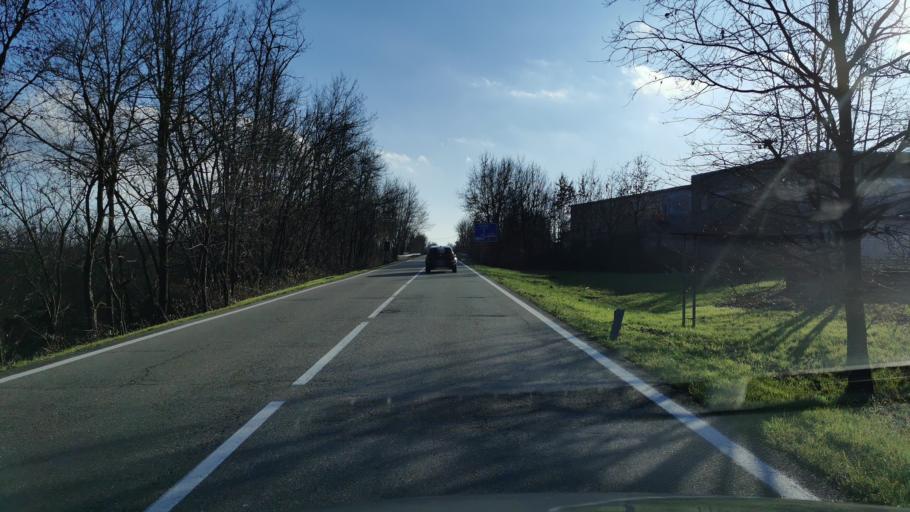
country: IT
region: Piedmont
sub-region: Provincia di Biella
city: Mottalciata
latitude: 45.4950
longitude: 8.2151
